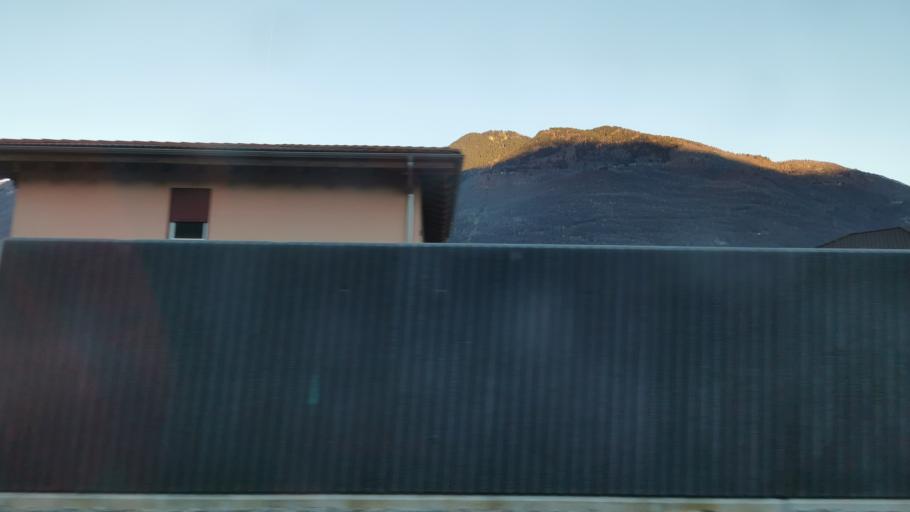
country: CH
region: Ticino
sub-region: Bellinzona District
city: Giubiasco
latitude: 46.1786
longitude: 9.0110
